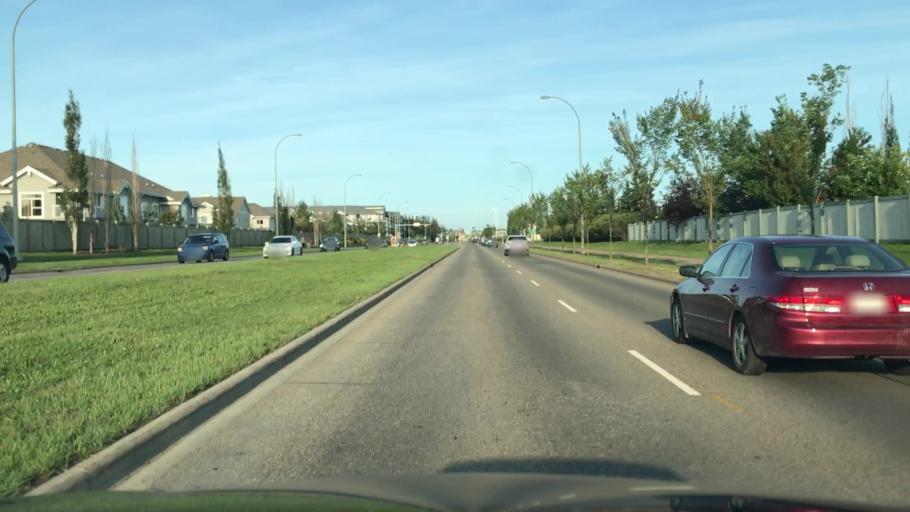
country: CA
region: Alberta
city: Beaumont
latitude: 53.4248
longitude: -113.4597
